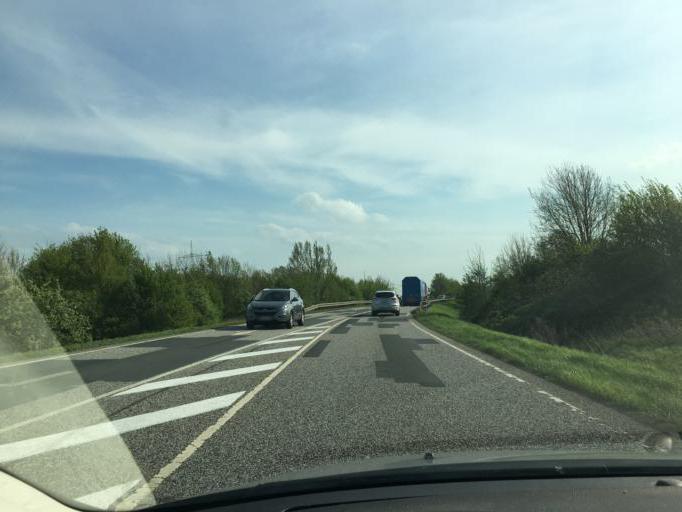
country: DE
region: Saxony-Anhalt
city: Meitzendorf
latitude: 52.2111
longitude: 11.5470
